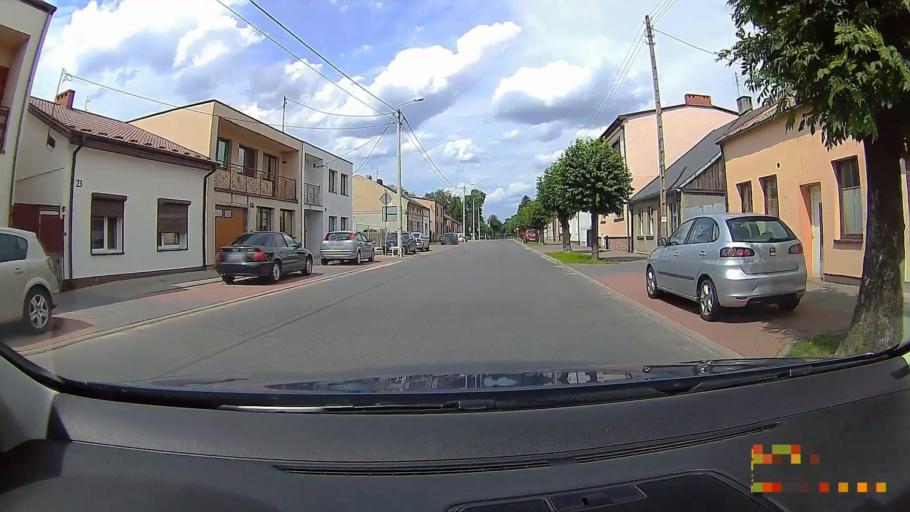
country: PL
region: Greater Poland Voivodeship
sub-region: Powiat koninski
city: Rychwal
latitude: 52.0716
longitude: 18.1650
